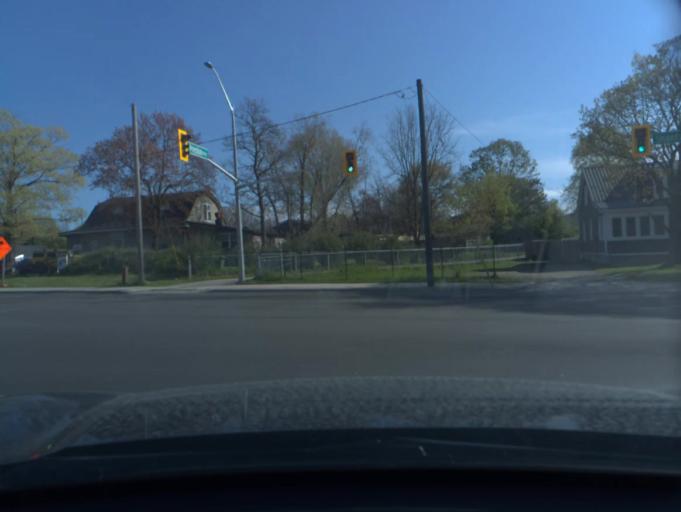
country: CA
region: Ontario
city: North Perth
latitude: 43.7989
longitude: -80.9999
